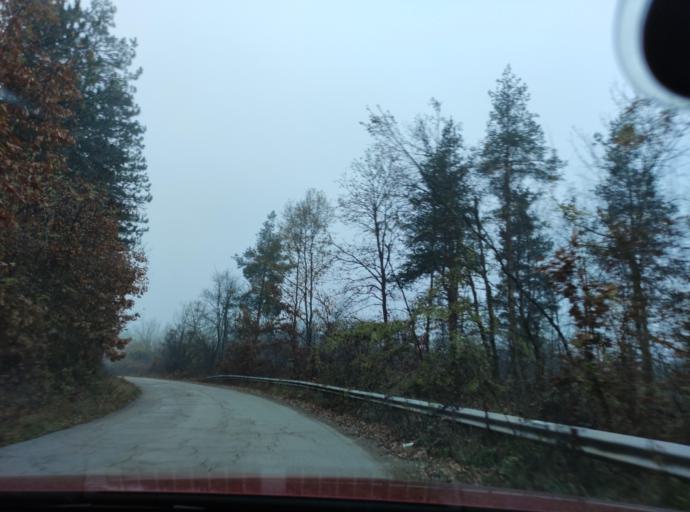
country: BG
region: Lovech
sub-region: Obshtina Yablanitsa
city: Yablanitsa
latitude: 43.1057
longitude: 24.0662
